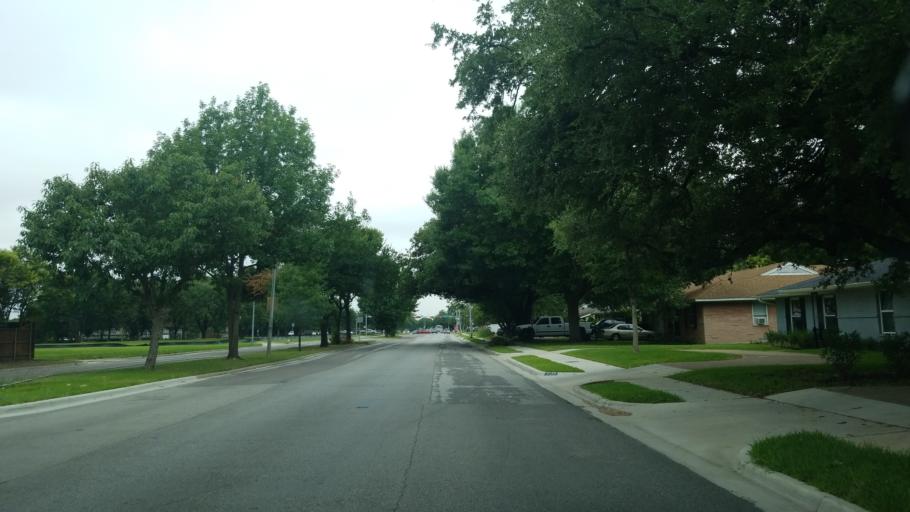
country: US
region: Texas
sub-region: Dallas County
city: Farmers Branch
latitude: 32.8953
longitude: -96.8678
